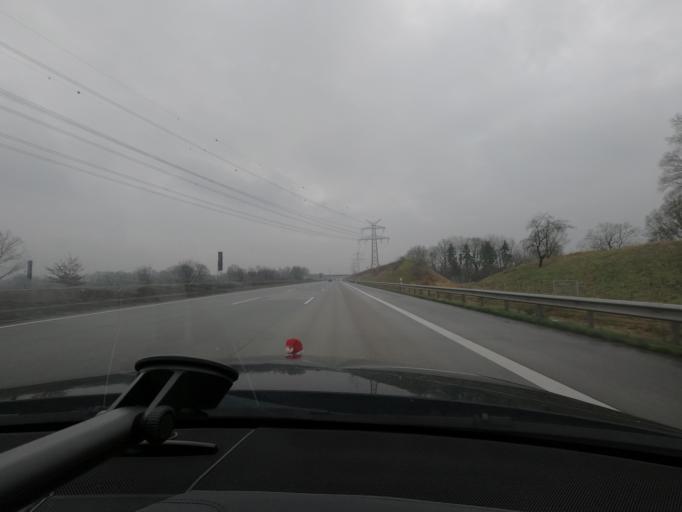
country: DE
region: Schleswig-Holstein
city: Alveslohe
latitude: 53.7948
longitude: 9.9336
